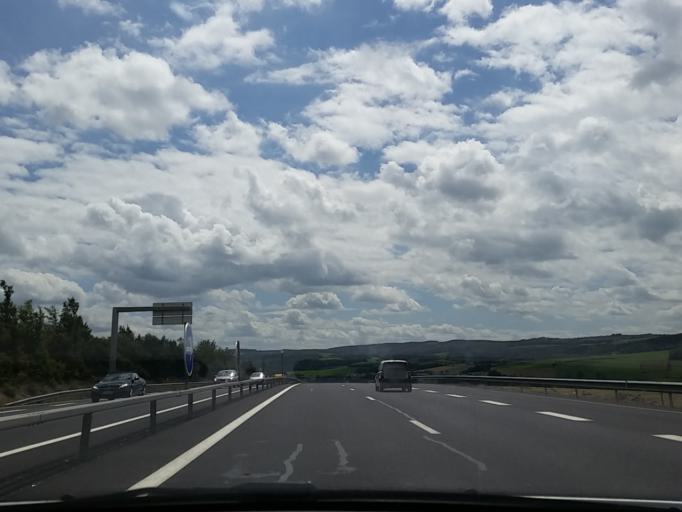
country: FR
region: Auvergne
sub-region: Departement du Cantal
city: Massiac
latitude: 45.1439
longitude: 3.1433
